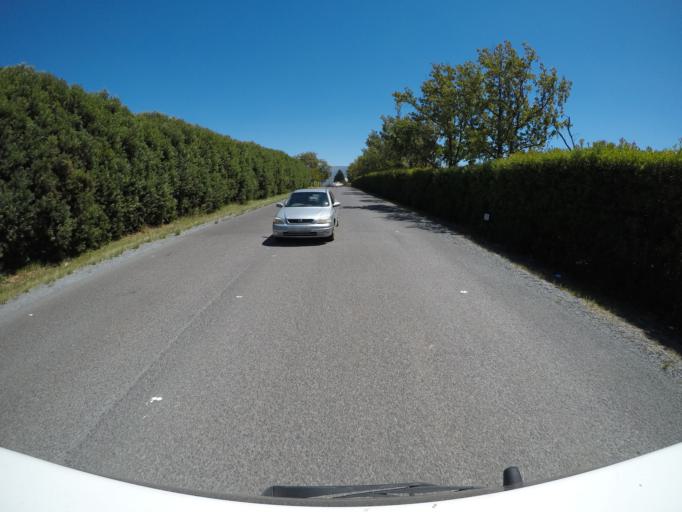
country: ZA
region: Western Cape
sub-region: Overberg District Municipality
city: Grabouw
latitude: -34.1819
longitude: 19.0377
